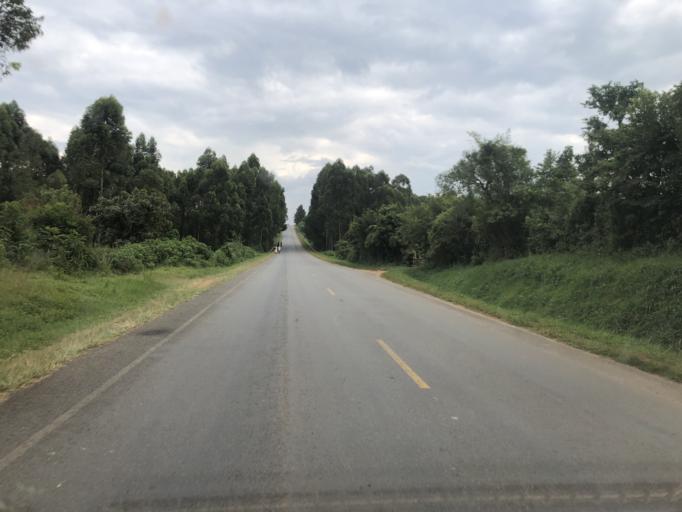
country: UG
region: Western Region
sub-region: Sheema District
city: Kibingo
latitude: -0.5790
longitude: 30.4131
